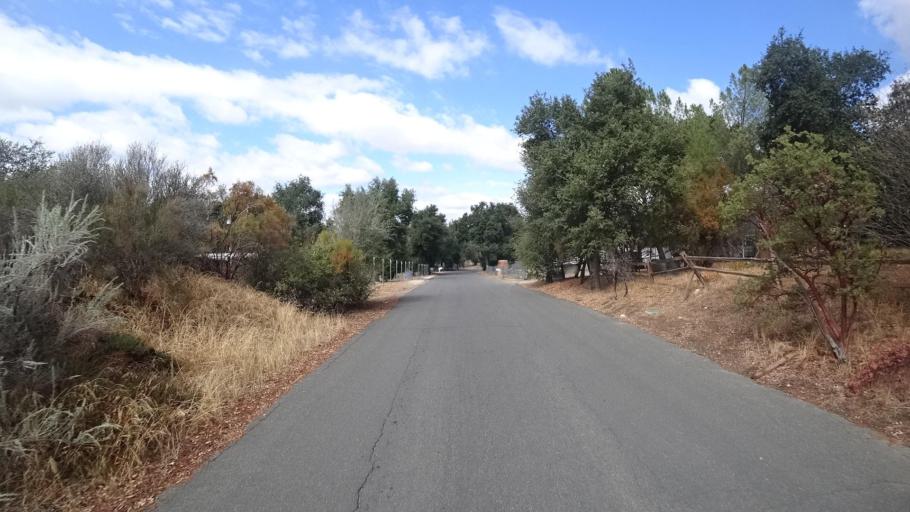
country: US
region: California
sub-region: San Diego County
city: Campo
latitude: 32.6844
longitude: -116.5129
